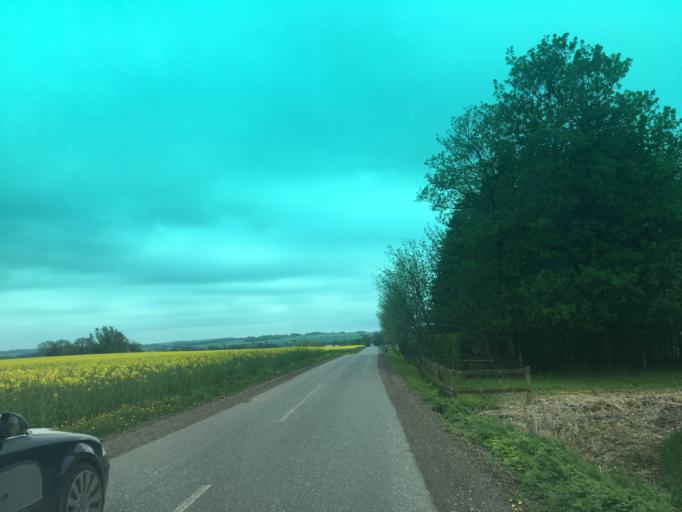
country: DK
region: Zealand
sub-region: Ringsted Kommune
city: Ringsted
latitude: 55.4249
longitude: 11.7115
